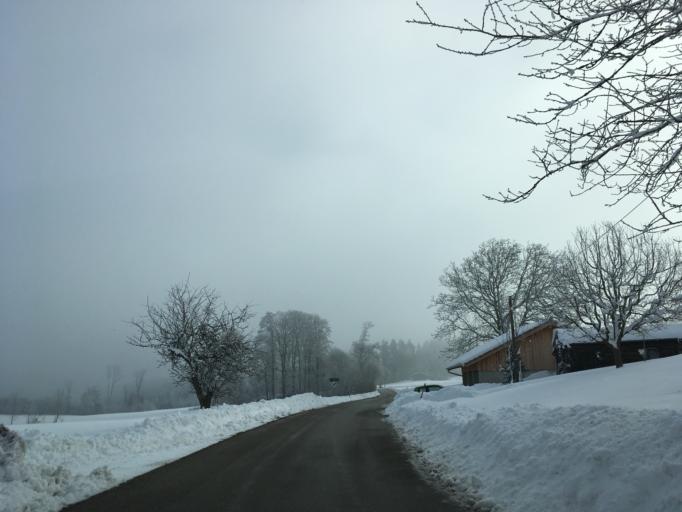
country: DE
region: Bavaria
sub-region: Upper Bavaria
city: Frasdorf
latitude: 47.8440
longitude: 12.2762
